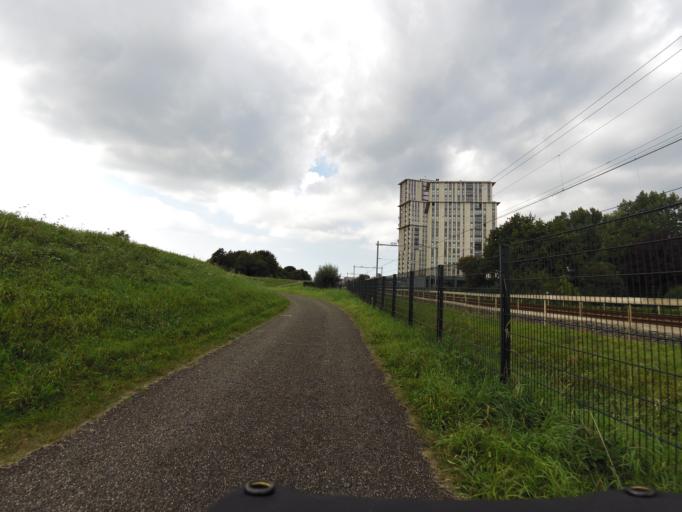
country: NL
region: South Holland
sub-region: Gemeente Maassluis
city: Maassluis
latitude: 51.9308
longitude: 4.2276
